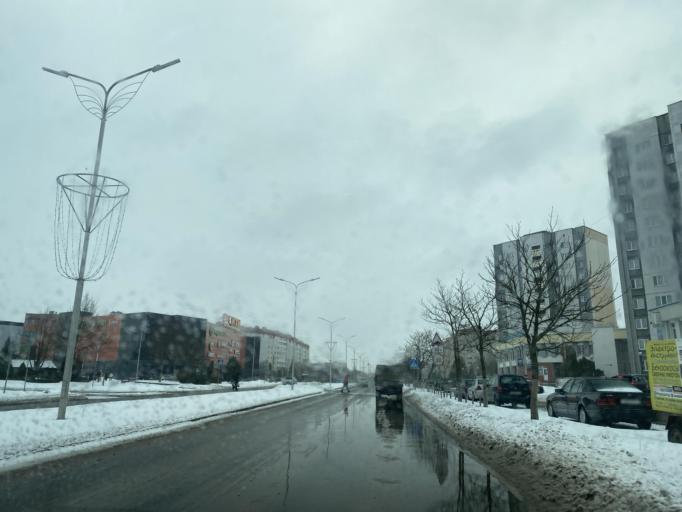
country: BY
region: Minsk
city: Horad Zhodzina
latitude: 54.0966
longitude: 28.3023
